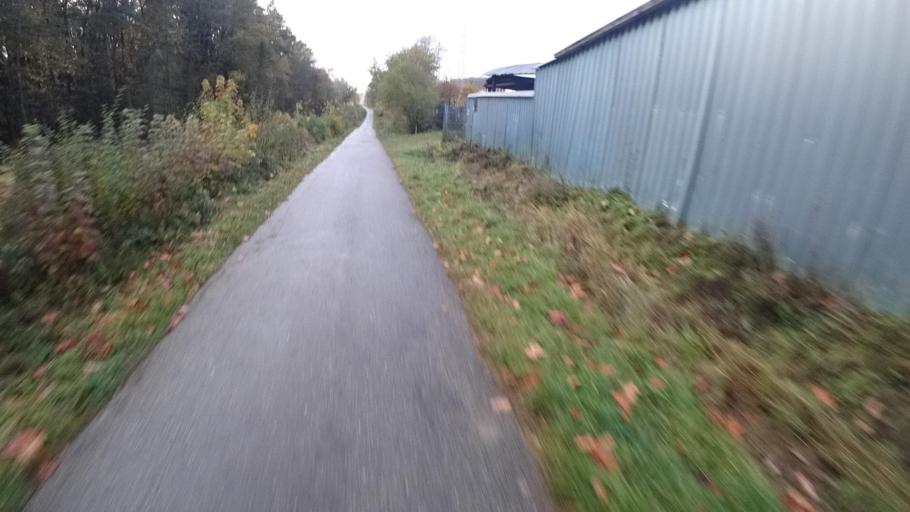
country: DE
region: Rheinland-Pfalz
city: Emmelshausen
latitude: 50.1636
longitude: 7.5639
